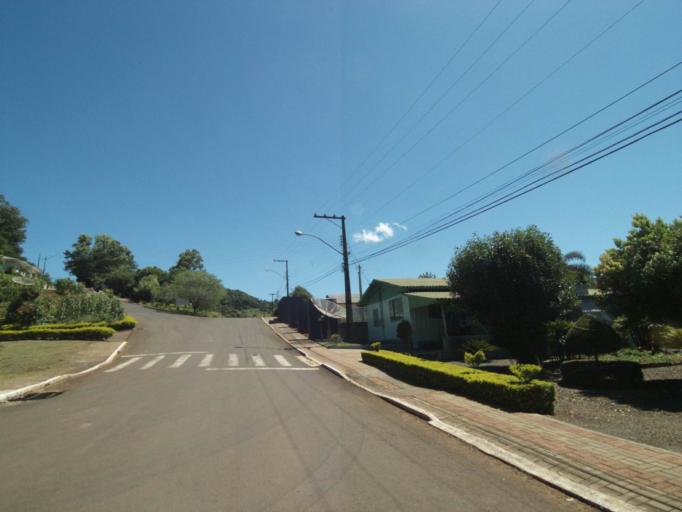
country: BR
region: Parana
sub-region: Ampere
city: Ampere
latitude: -26.1738
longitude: -53.3605
